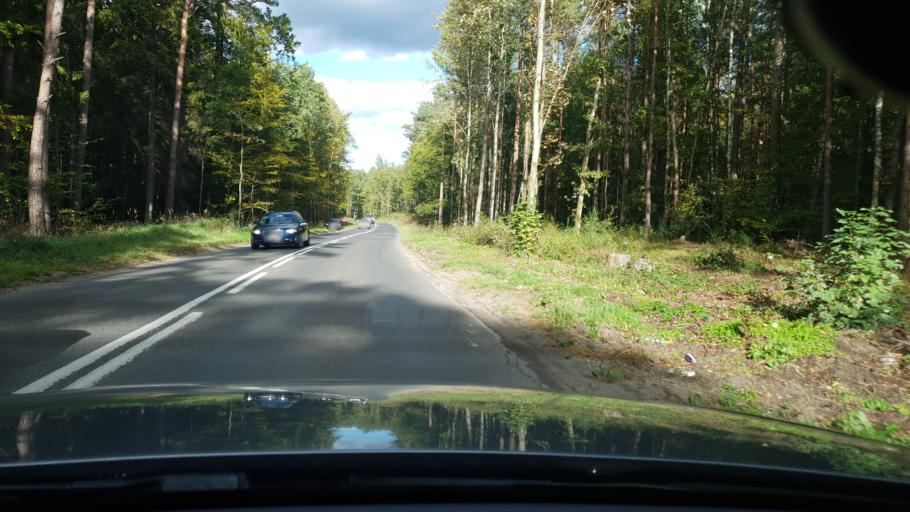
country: PL
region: Pomeranian Voivodeship
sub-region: Powiat wejherowski
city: Koleczkowo
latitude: 54.5011
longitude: 18.3645
